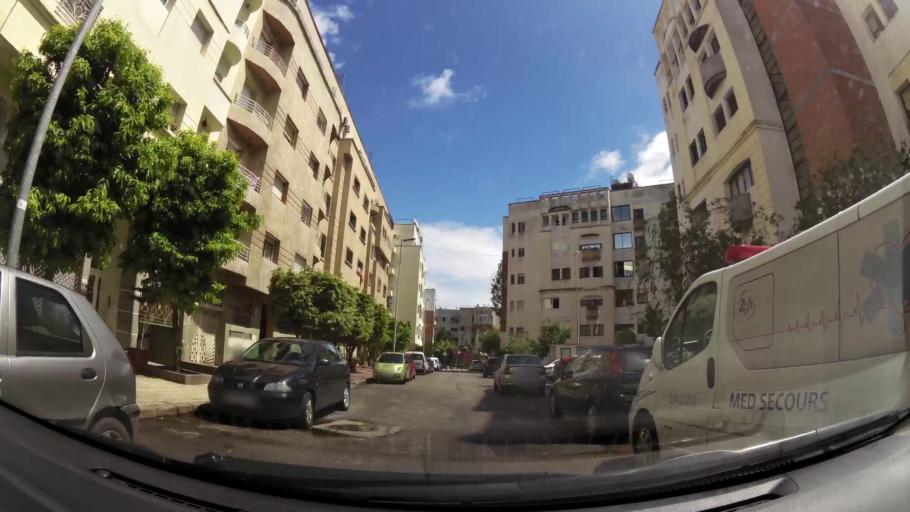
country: MA
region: Grand Casablanca
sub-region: Casablanca
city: Casablanca
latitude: 33.5593
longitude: -7.6746
